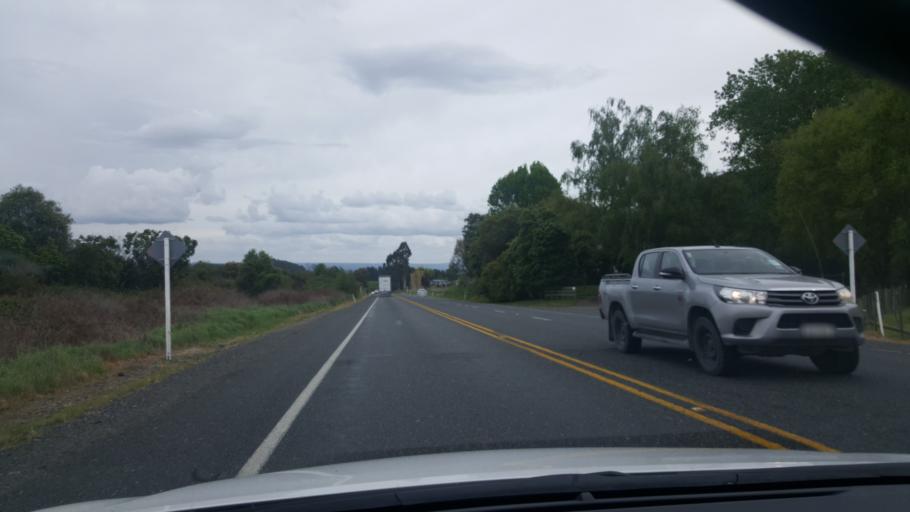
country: NZ
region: Bay of Plenty
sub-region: Rotorua District
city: Rotorua
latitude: -38.3462
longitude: 176.3611
